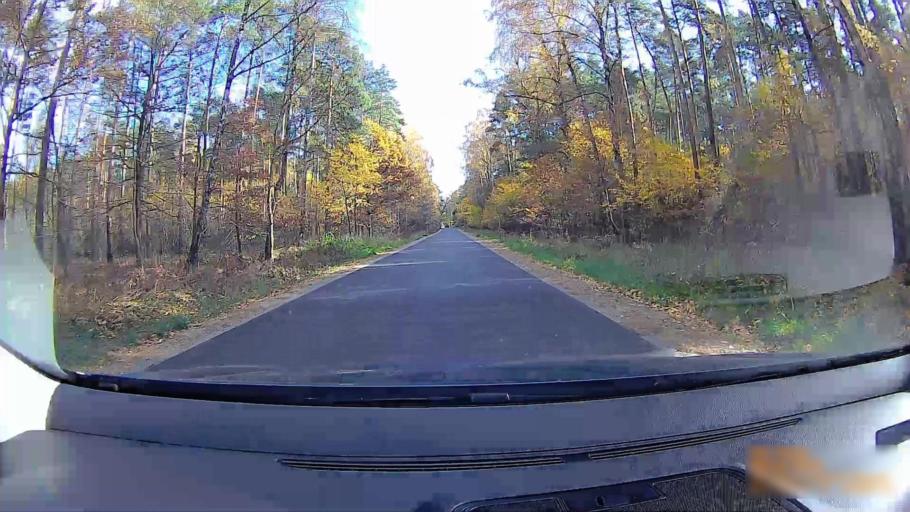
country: PL
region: Greater Poland Voivodeship
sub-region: Powiat ostrzeszowski
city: Doruchow
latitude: 51.4062
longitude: 18.0052
